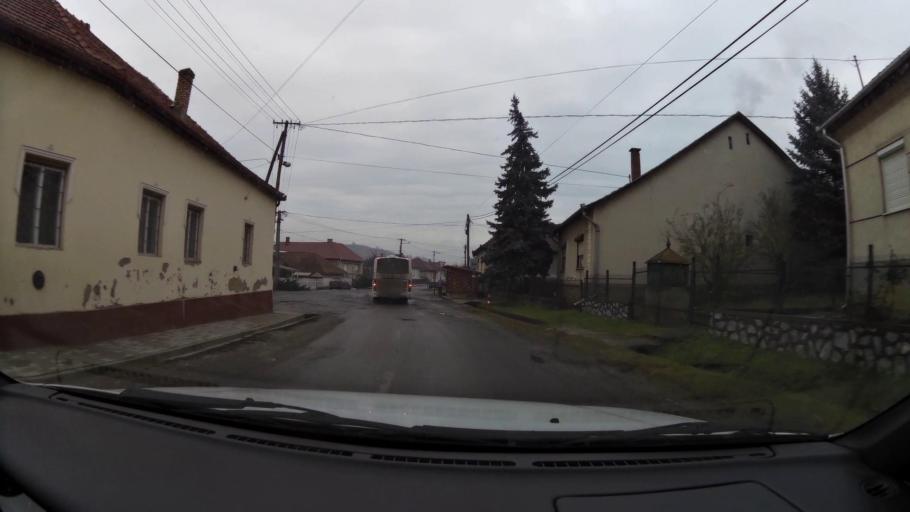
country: HU
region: Borsod-Abauj-Zemplen
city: Rudabanya
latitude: 48.4069
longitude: 20.6358
